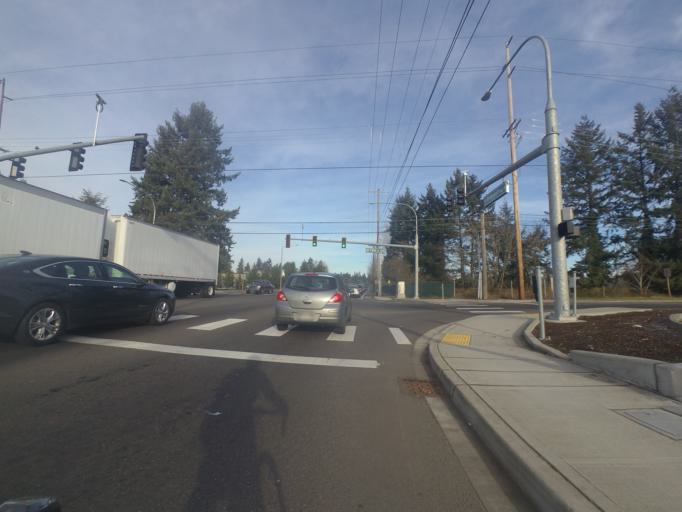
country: US
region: Washington
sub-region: Pierce County
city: Lakewood
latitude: 47.1891
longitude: -122.5184
